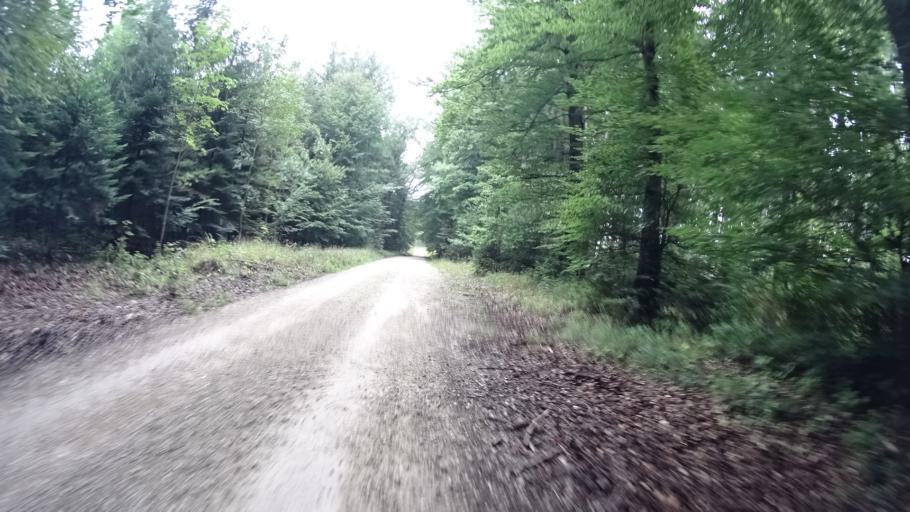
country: DE
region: Bavaria
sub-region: Upper Bavaria
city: Stammham
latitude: 48.8841
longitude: 11.5103
